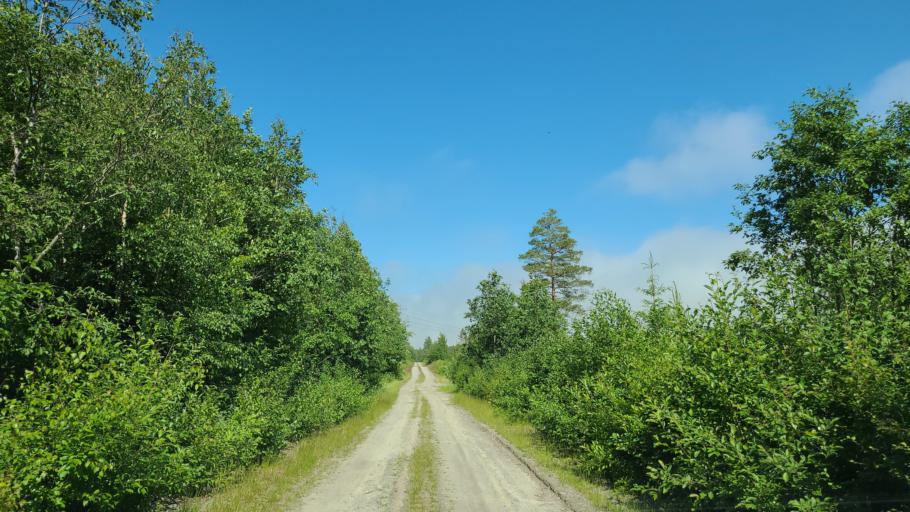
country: SE
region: Vaesternorrland
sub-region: OErnskoeldsviks Kommun
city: Husum
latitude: 63.4399
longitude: 19.2333
